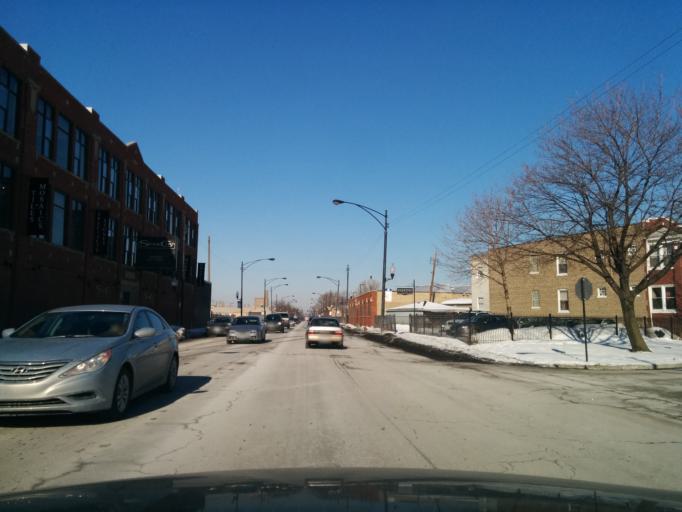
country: US
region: Illinois
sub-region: Cook County
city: Chicago
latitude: 41.8968
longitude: -87.7028
